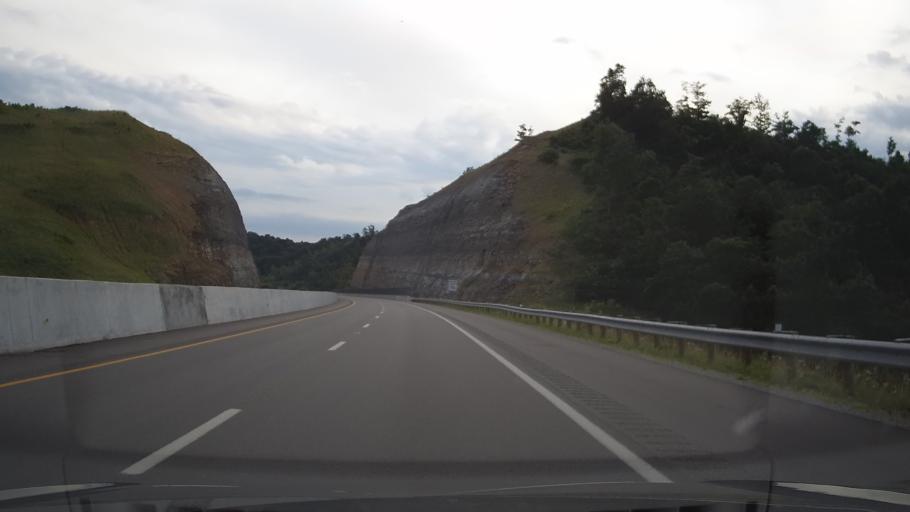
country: US
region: Ohio
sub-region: Scioto County
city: Lucasville
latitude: 38.8980
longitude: -82.9655
